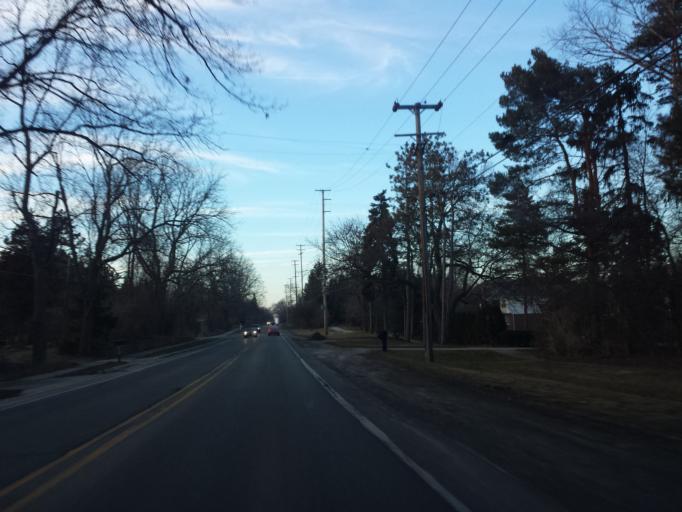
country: US
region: Michigan
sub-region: Oakland County
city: Bloomfield Hills
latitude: 42.5916
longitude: -83.2079
